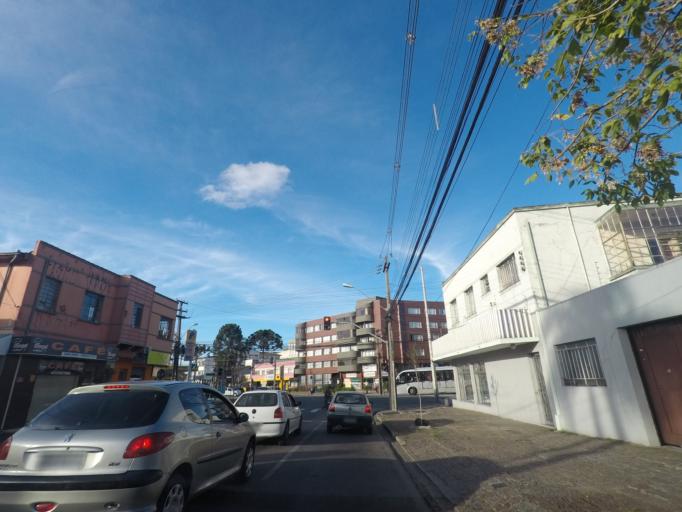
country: BR
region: Parana
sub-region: Curitiba
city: Curitiba
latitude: -25.4223
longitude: -49.2922
